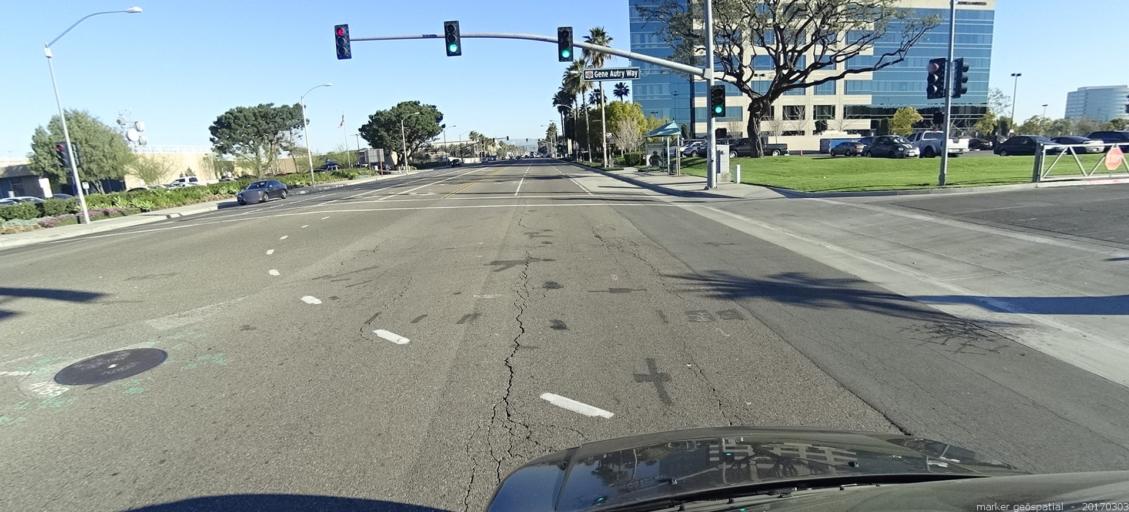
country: US
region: California
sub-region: Orange County
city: Orange
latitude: 33.7996
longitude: -117.8891
